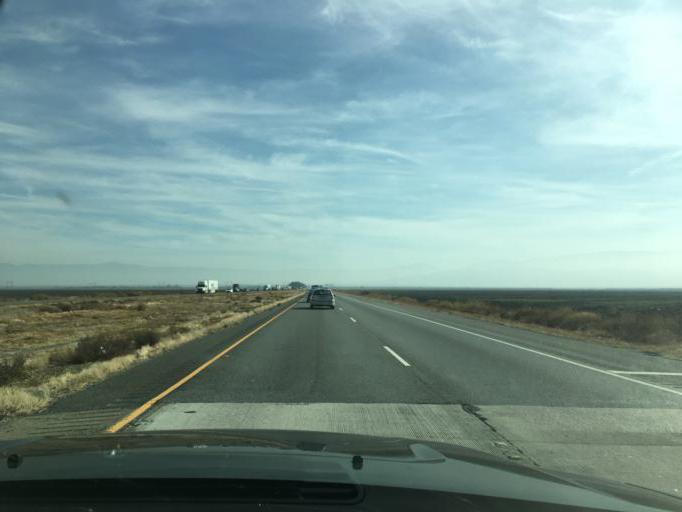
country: US
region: California
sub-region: Kern County
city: Greenfield
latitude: 35.1288
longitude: -119.0747
